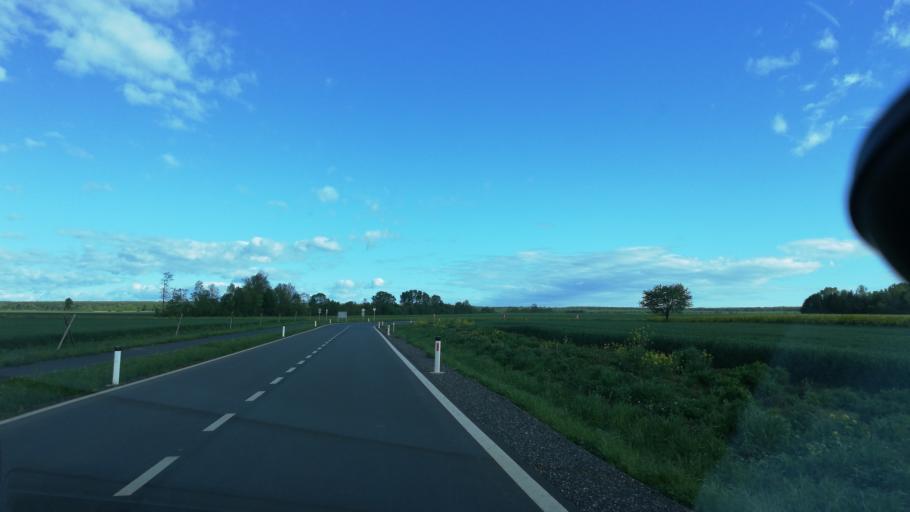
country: AT
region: Burgenland
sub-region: Politischer Bezirk Oberpullendorf
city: Lutzmannsburg
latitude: 47.4666
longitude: 16.6508
